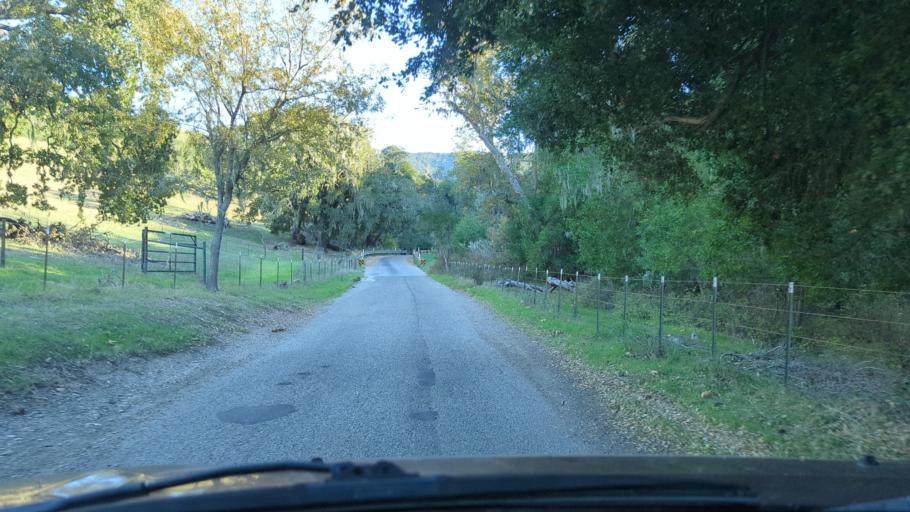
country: US
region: California
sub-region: Santa Barbara County
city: Santa Ynez
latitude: 34.5609
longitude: -120.0861
